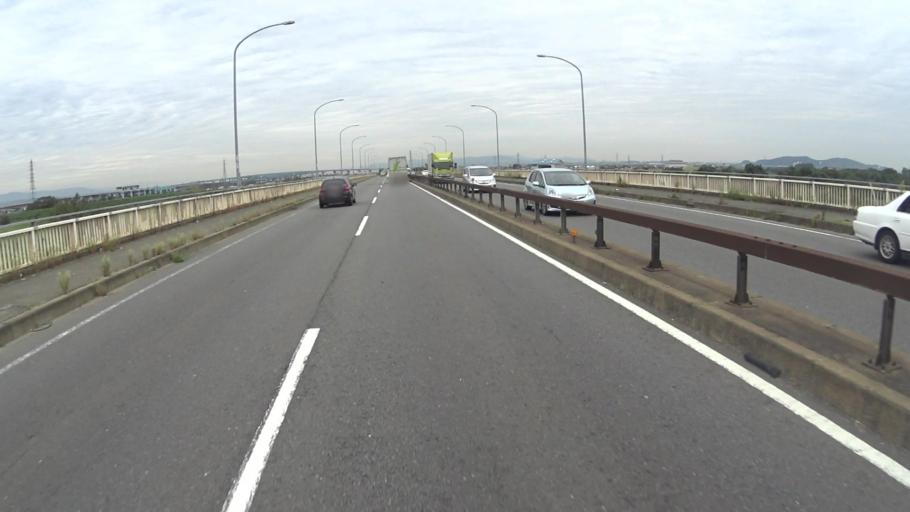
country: JP
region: Kyoto
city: Muko
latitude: 34.9186
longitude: 135.7449
